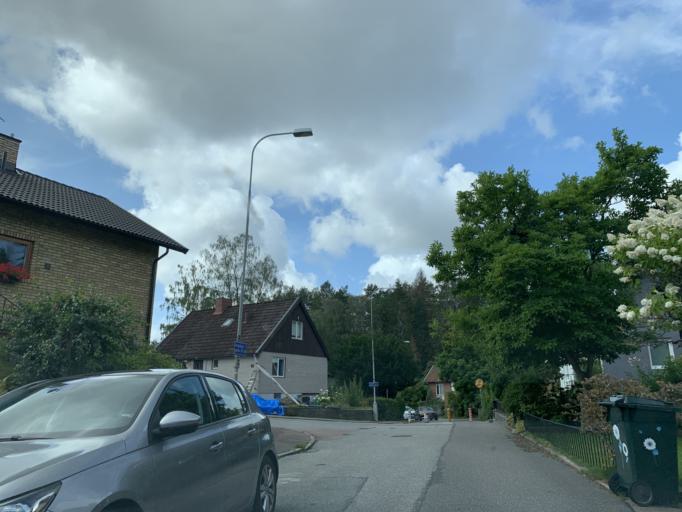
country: SE
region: Vaestra Goetaland
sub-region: Goteborg
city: Eriksbo
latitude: 57.7599
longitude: 12.0315
